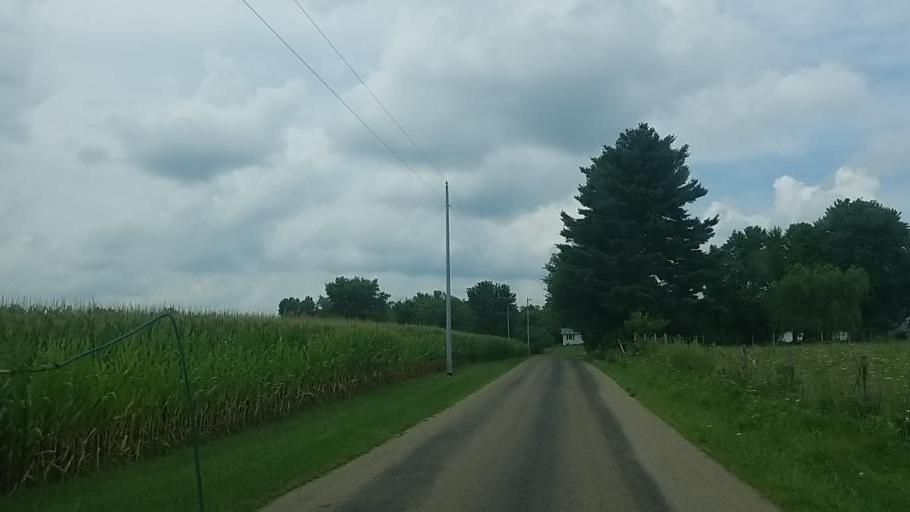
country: US
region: Ohio
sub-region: Knox County
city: Gambier
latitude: 40.3388
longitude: -82.4309
